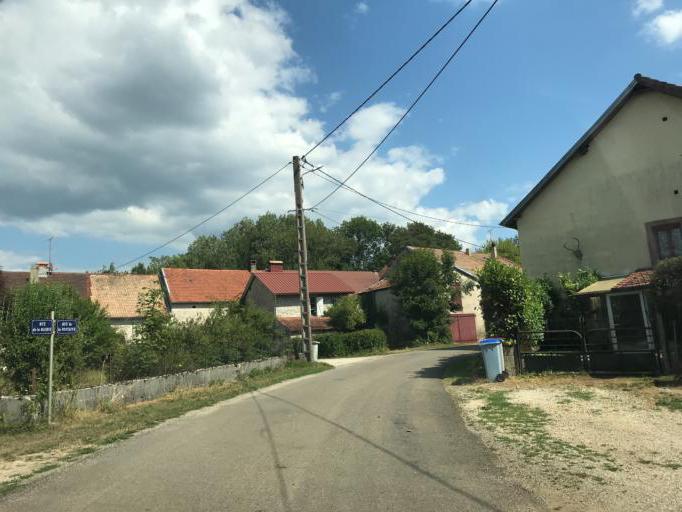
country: FR
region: Franche-Comte
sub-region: Departement du Jura
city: Clairvaux-les-Lacs
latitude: 46.5924
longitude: 5.7370
